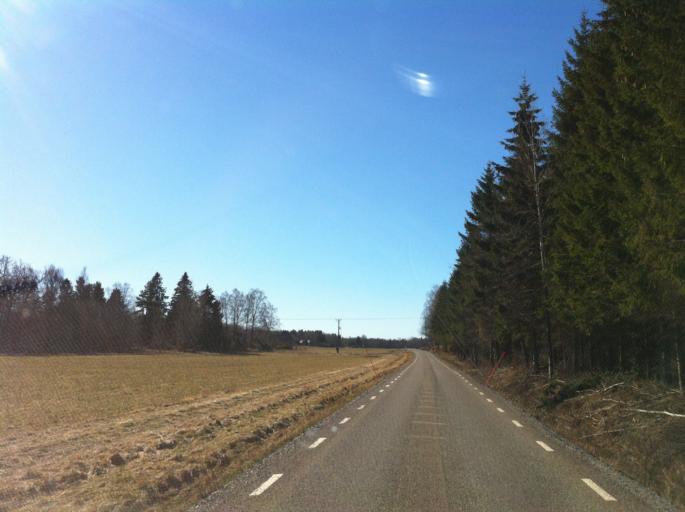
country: SE
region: Vaestra Goetaland
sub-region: Grastorps Kommun
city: Graestorp
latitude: 58.4525
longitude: 12.6173
